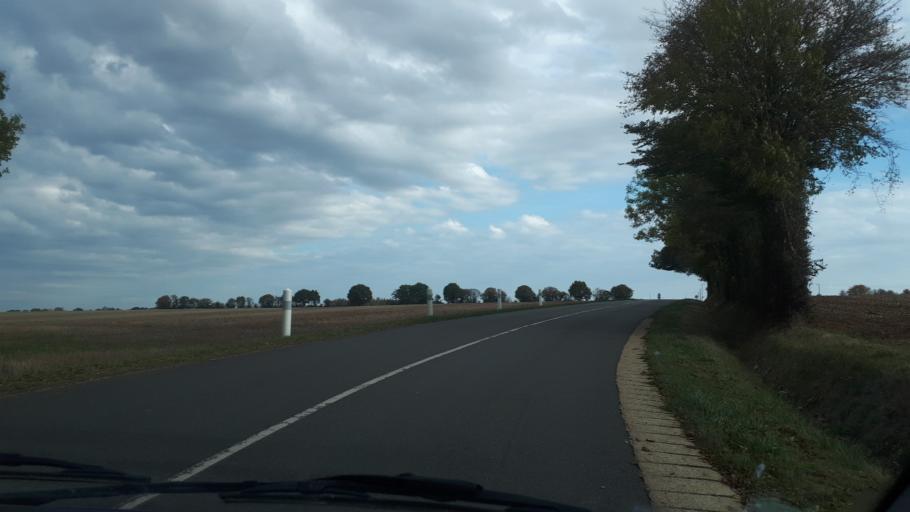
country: FR
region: Centre
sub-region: Departement du Loir-et-Cher
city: Mondoubleau
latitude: 48.0035
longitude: 0.9149
